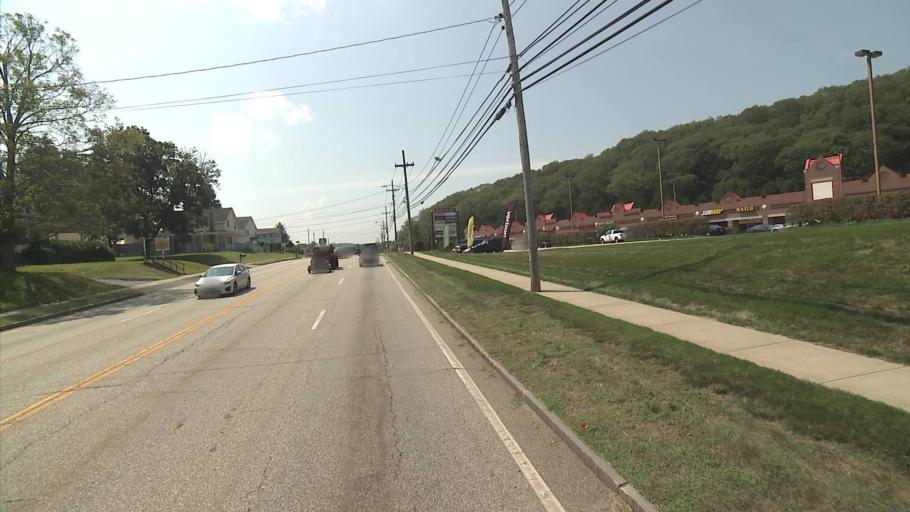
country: US
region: Connecticut
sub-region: New London County
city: Norwich
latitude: 41.5127
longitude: -72.1098
